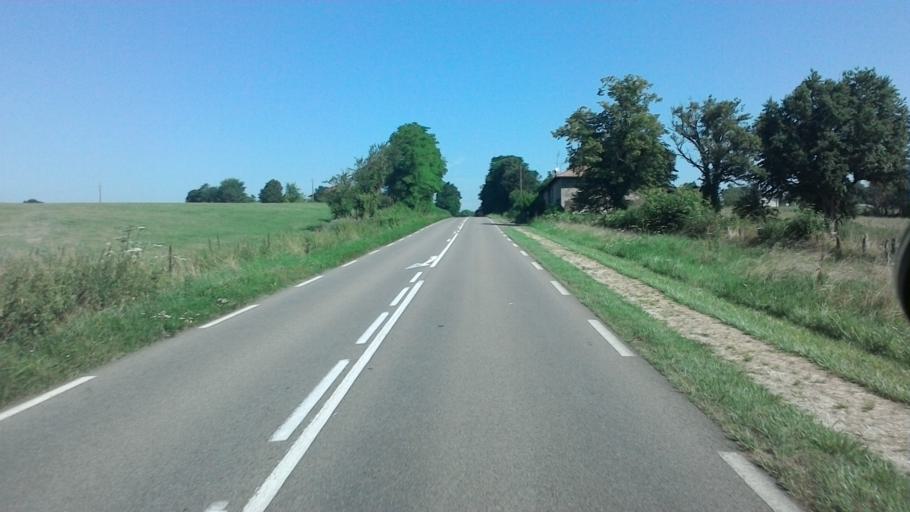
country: FR
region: Rhone-Alpes
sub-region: Departement de l'Ain
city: Saint-Trivier-de-Courtes
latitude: 46.4284
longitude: 5.0970
